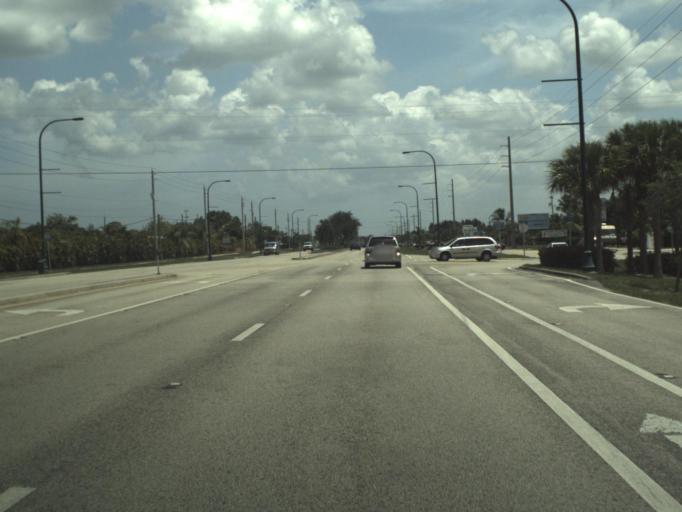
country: US
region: Florida
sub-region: Martin County
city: Hobe Sound
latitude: 27.0711
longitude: -80.1418
